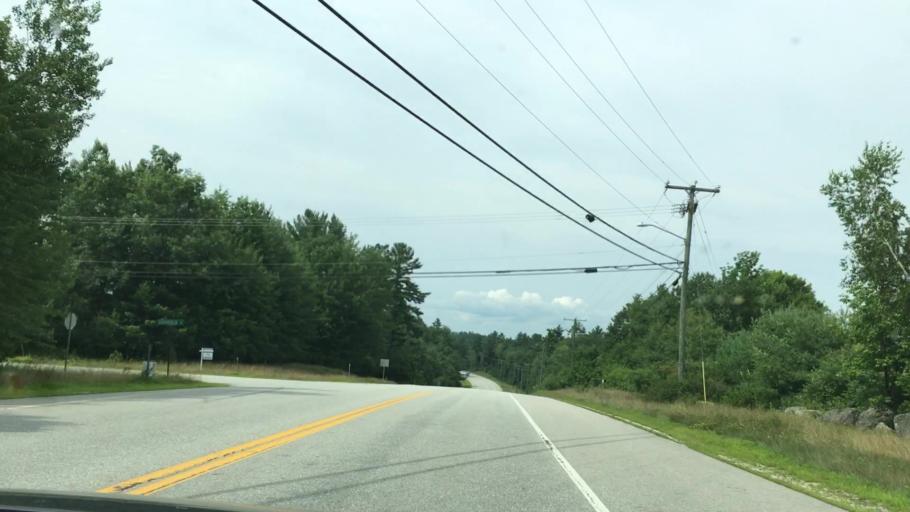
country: US
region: New Hampshire
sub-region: Hillsborough County
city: Peterborough
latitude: 42.9149
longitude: -71.9393
